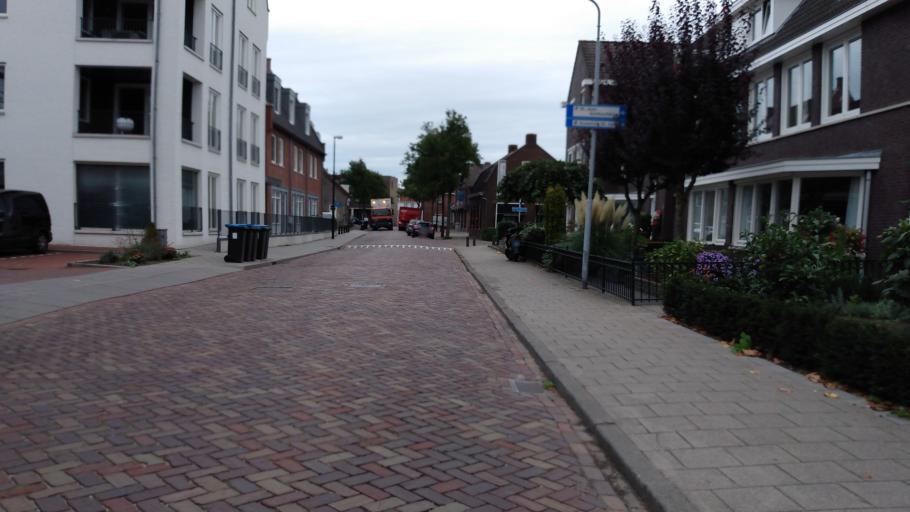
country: NL
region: North Brabant
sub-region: Gemeente Oisterwijk
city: Oisterwijk
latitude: 51.5432
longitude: 5.1824
